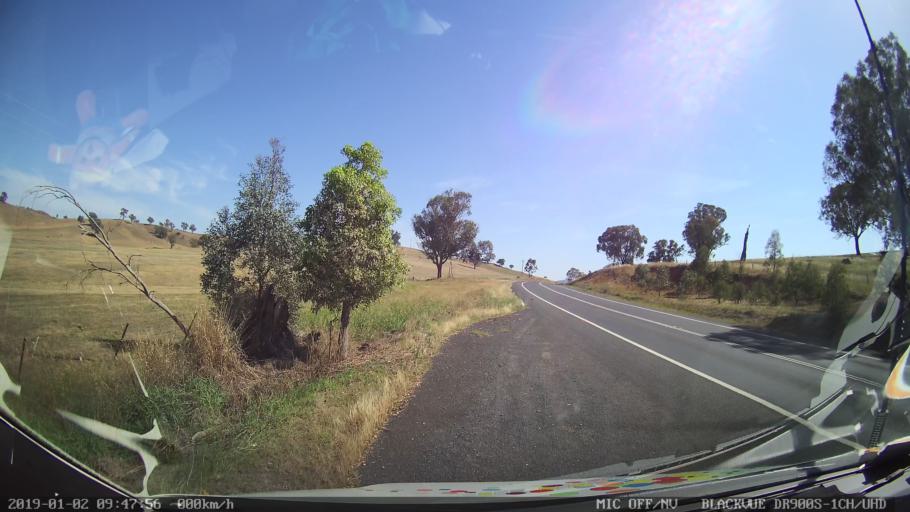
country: AU
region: New South Wales
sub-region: Tumut Shire
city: Tumut
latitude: -35.2803
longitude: 148.2058
